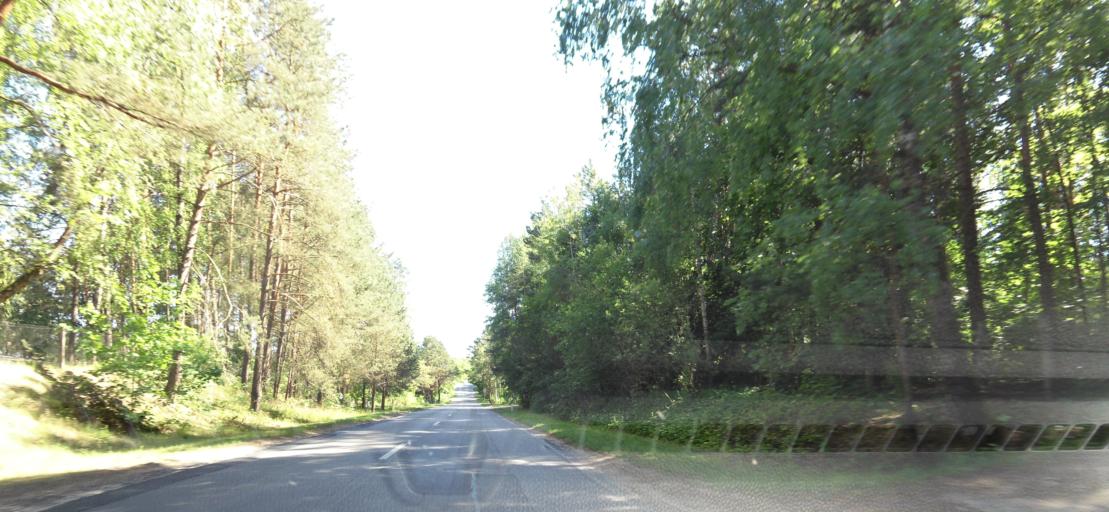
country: LT
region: Vilnius County
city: Rasos
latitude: 54.7943
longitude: 25.3504
